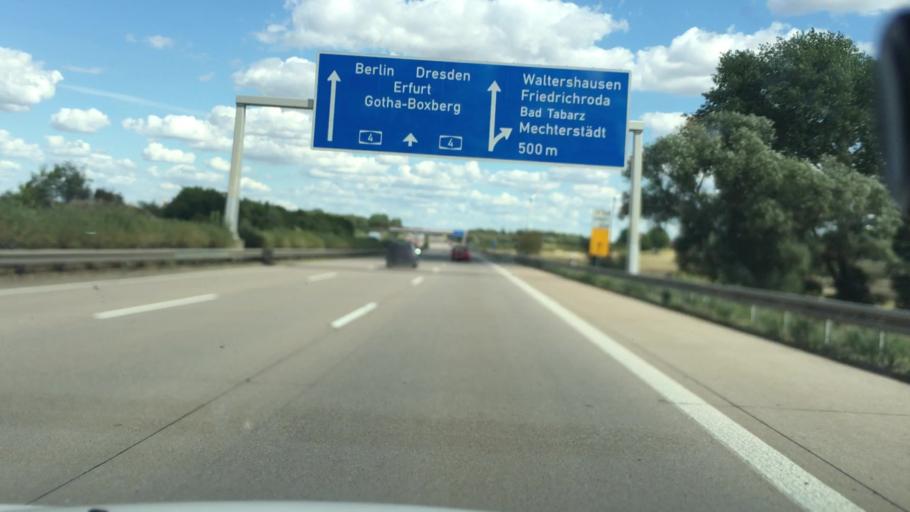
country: DE
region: Thuringia
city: Mechterstadt
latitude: 50.9202
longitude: 10.5398
